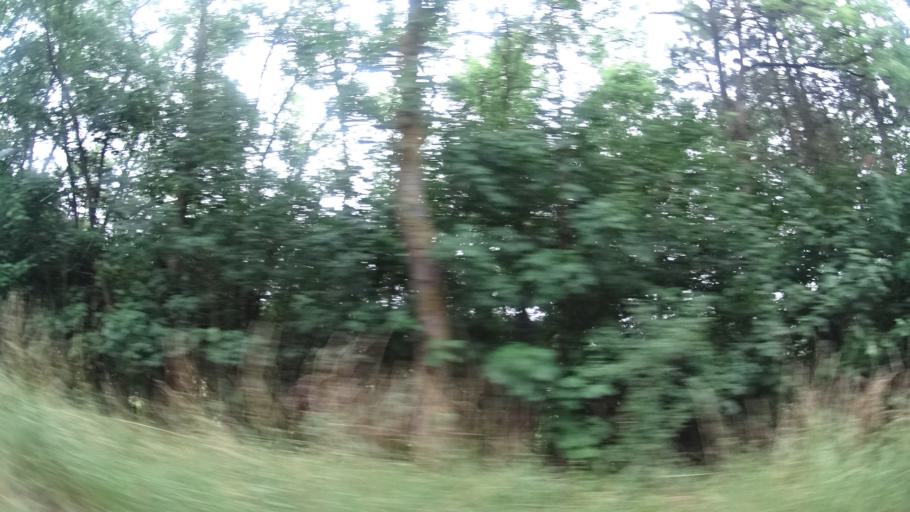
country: LU
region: Luxembourg
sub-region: Canton d'Esch-sur-Alzette
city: Sanem
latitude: 49.5540
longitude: 5.9264
